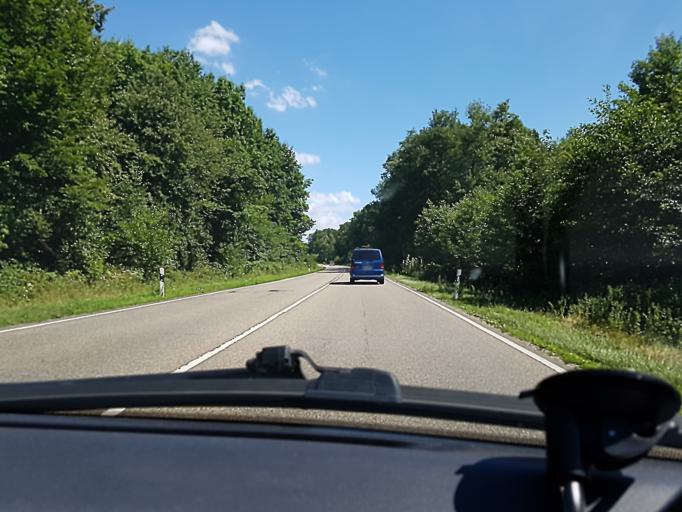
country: DE
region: Baden-Wuerttemberg
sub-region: Freiburg Region
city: Schutterwald
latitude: 48.4746
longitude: 7.8961
